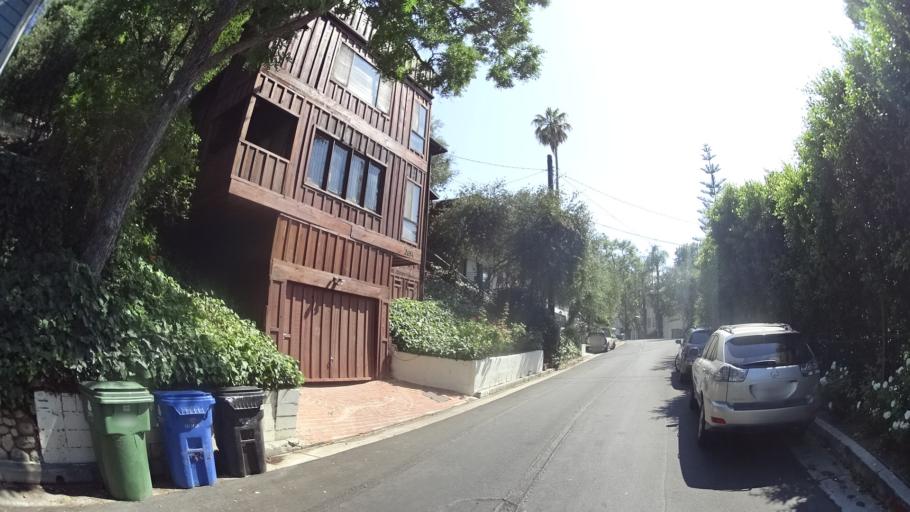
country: US
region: California
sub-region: Los Angeles County
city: Universal City
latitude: 34.1379
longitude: -118.3880
